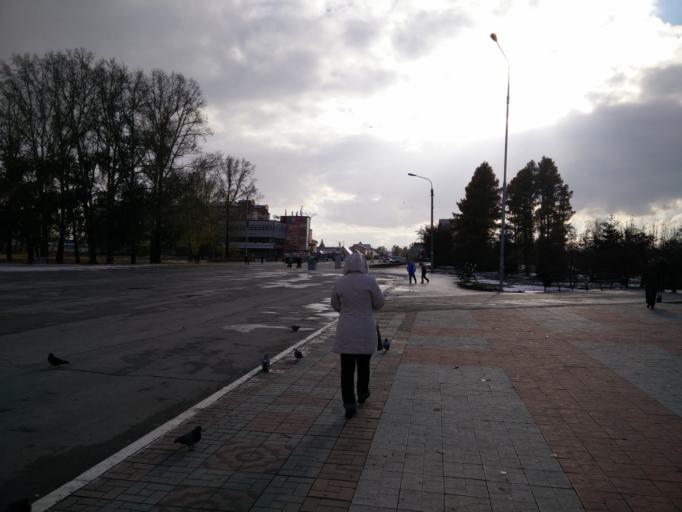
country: RU
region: Novosibirsk
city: Berdsk
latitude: 54.7580
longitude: 83.1063
